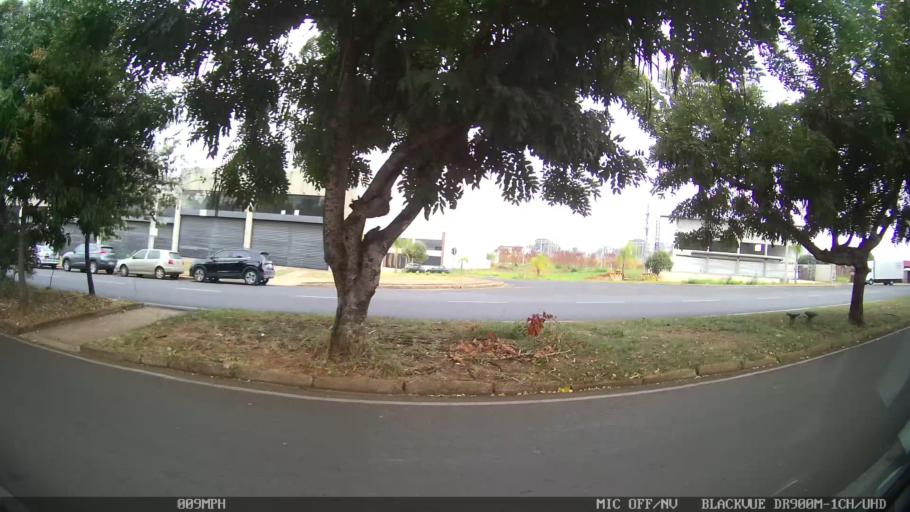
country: BR
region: Sao Paulo
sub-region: Sao Jose Do Rio Preto
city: Sao Jose do Rio Preto
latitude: -20.8435
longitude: -49.3704
